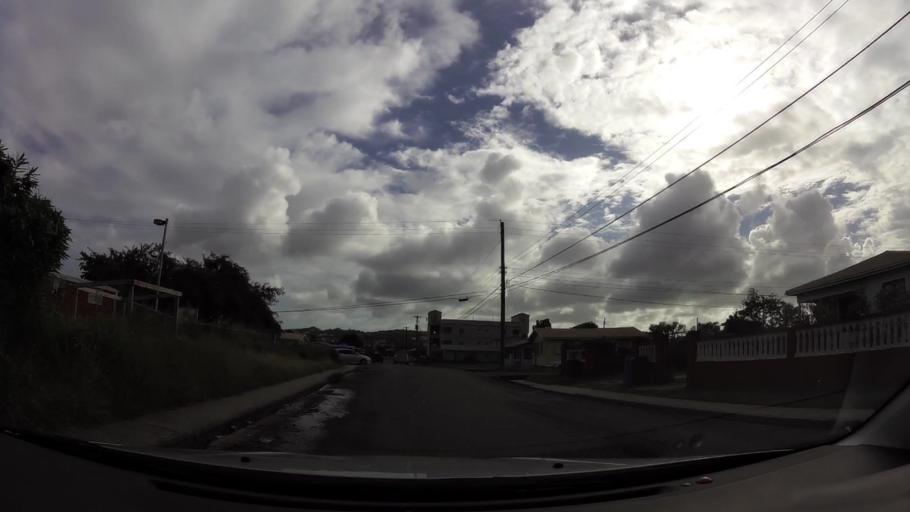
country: AG
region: Saint John
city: Saint John's
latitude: 17.1271
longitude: -61.8228
